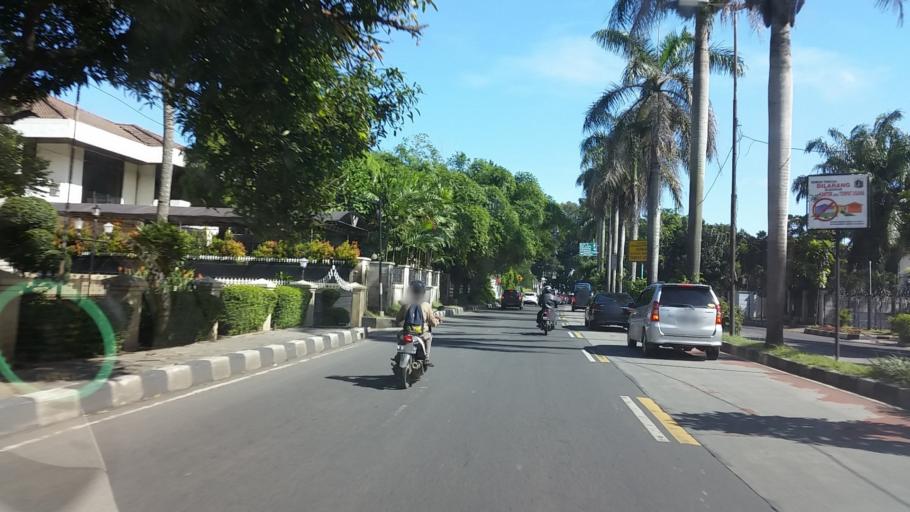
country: ID
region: Banten
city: South Tangerang
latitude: -6.2822
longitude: 106.7802
